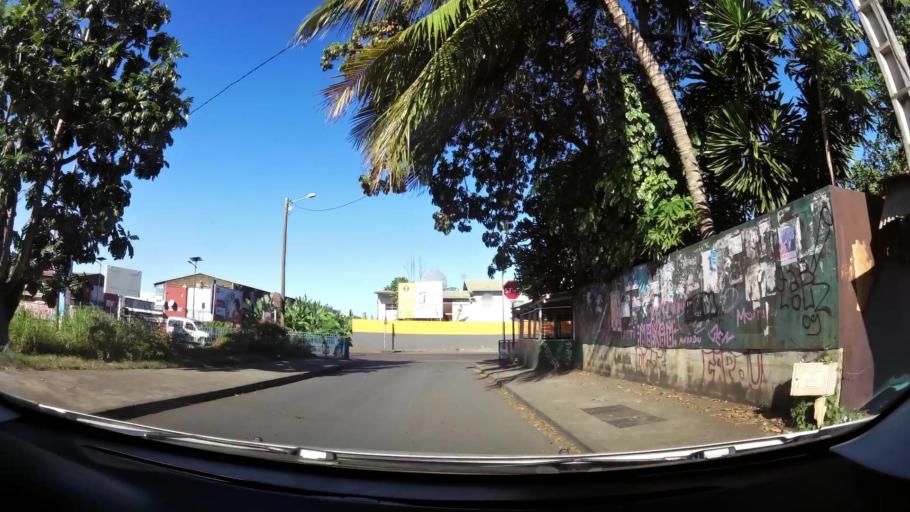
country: YT
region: Mamoudzou
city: Mamoudzou
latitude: -12.7724
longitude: 45.2230
